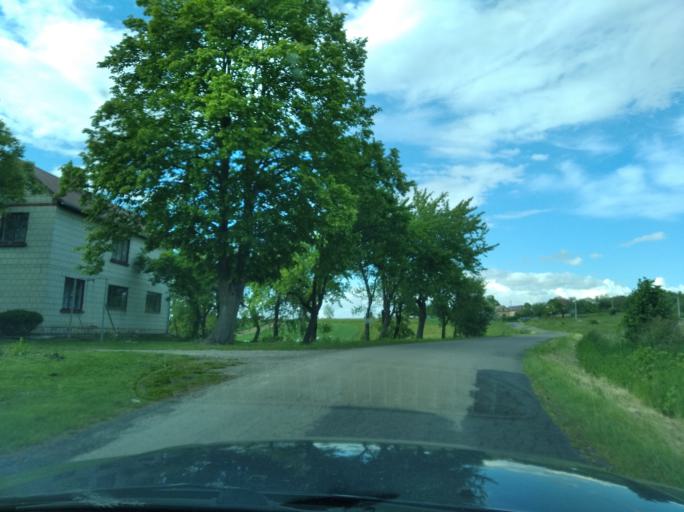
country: PL
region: Subcarpathian Voivodeship
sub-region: Powiat przemyski
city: Przedmiescie Dubieckie
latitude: 49.8854
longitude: 22.3707
